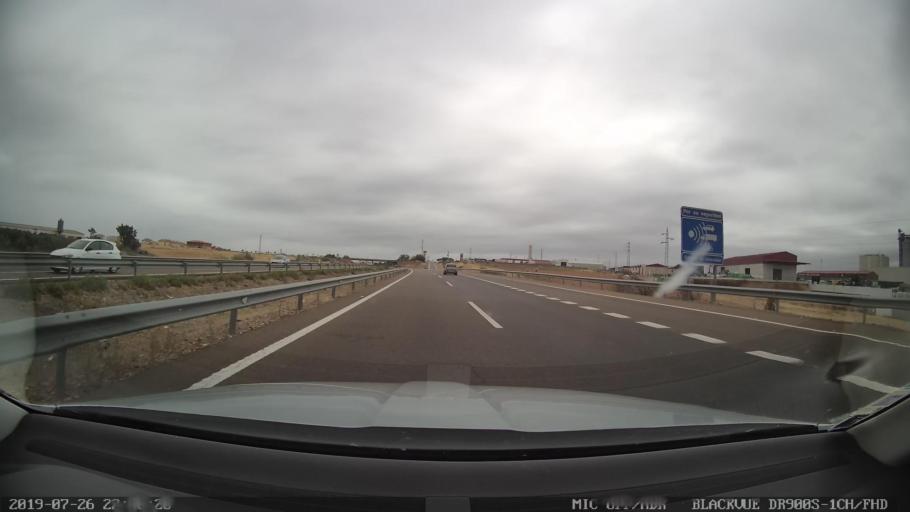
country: ES
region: Extremadura
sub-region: Provincia de Badajoz
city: Lobon
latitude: 38.8411
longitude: -6.6241
